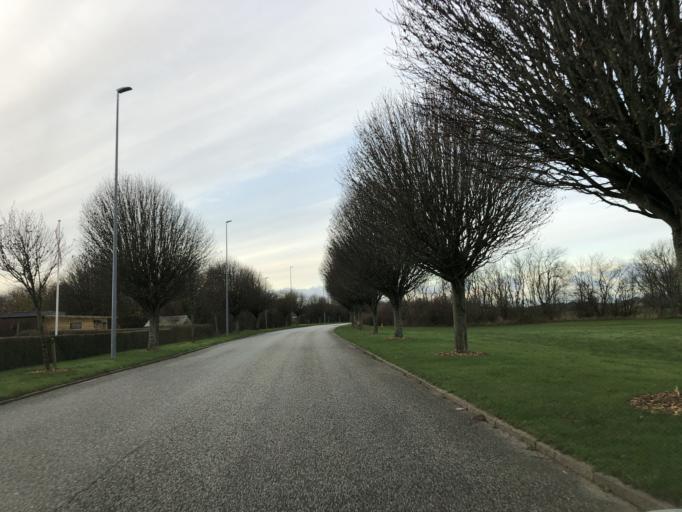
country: DK
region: Central Jutland
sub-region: Struer Kommune
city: Struer
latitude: 56.4839
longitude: 8.5721
